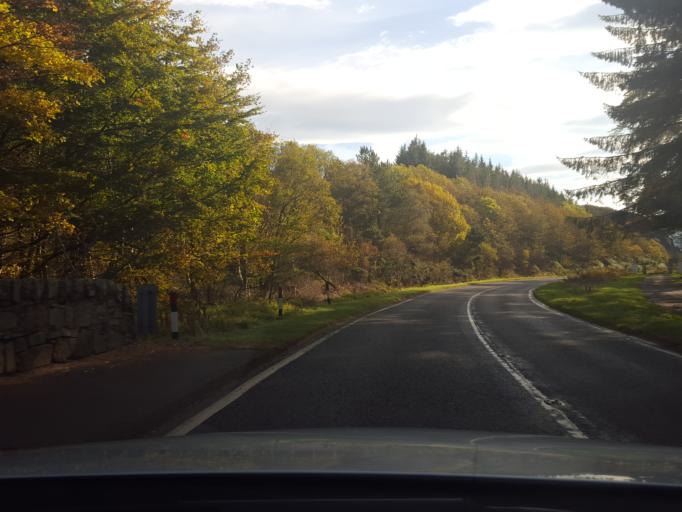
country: GB
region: Scotland
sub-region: Highland
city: Portree
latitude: 57.2875
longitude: -5.6434
